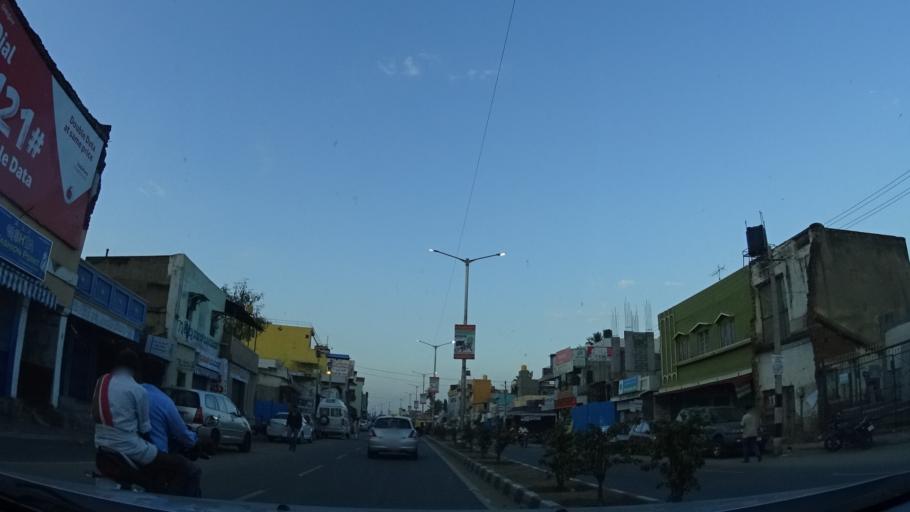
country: IN
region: Karnataka
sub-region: Ramanagara
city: Kanakapura
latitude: 12.5496
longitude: 77.4239
